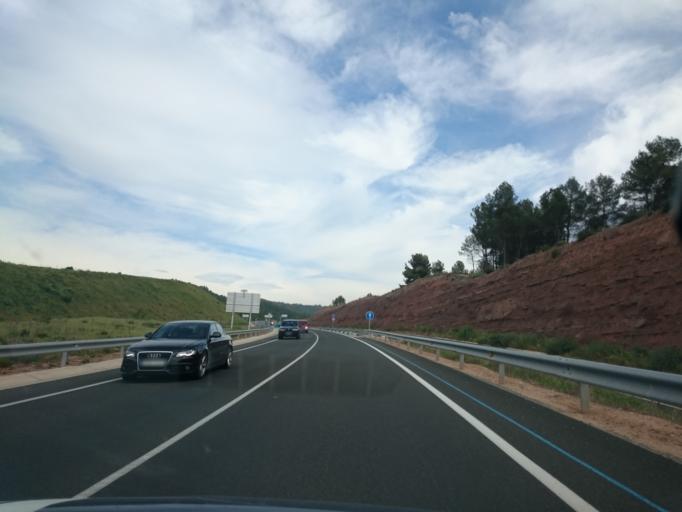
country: ES
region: Catalonia
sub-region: Provincia de Barcelona
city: Sant Salvador de Guardiola
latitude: 41.6964
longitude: 1.7808
